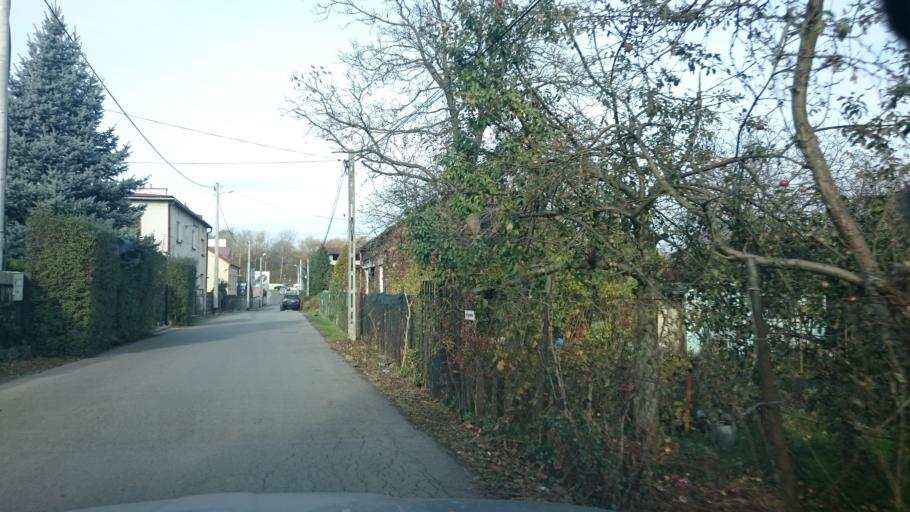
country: PL
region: Lesser Poland Voivodeship
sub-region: Krakow
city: Krakow
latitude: 50.0257
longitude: 19.9648
